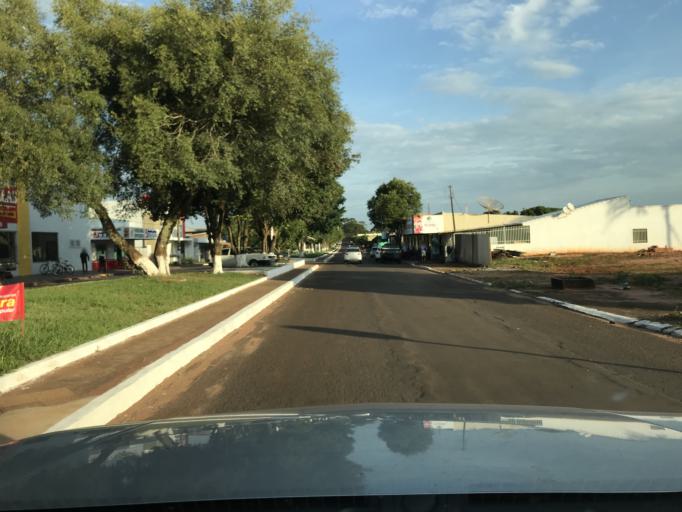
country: BR
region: Mato Grosso do Sul
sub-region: Iguatemi
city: Iguatemi
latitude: -23.6658
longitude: -54.5624
